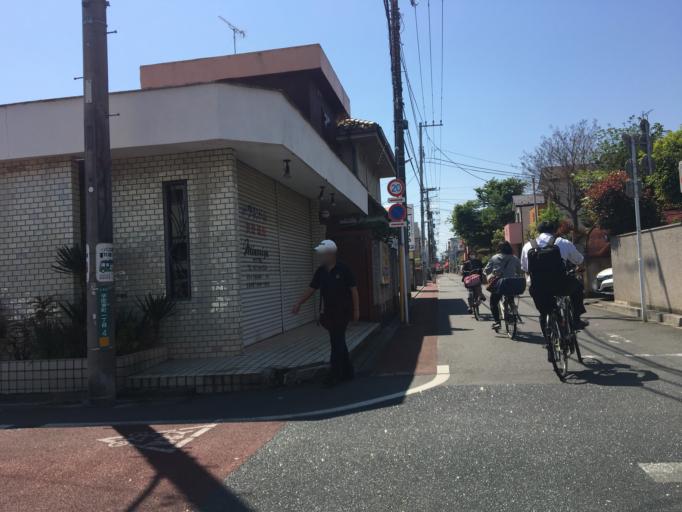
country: JP
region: Tokyo
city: Kokubunji
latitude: 35.7239
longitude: 139.4828
